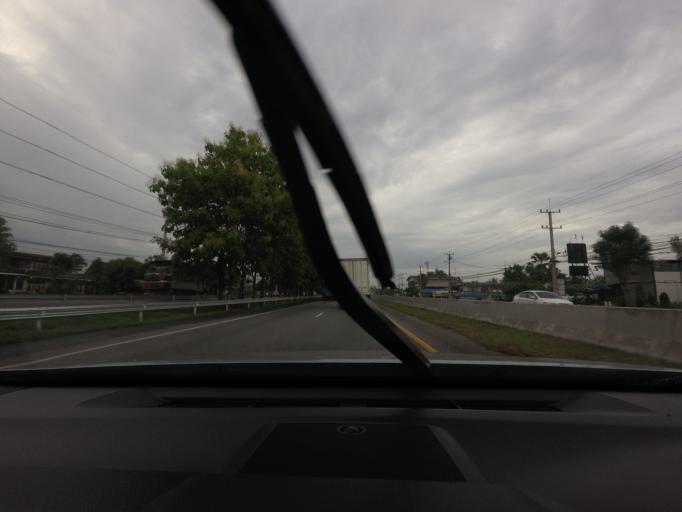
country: TH
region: Phetchaburi
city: Khao Yoi
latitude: 13.2615
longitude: 99.8229
